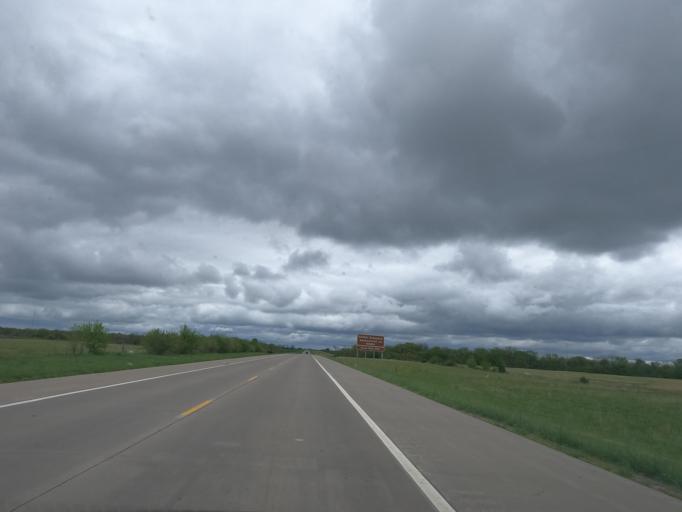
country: US
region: Kansas
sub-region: Labette County
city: Parsons
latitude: 37.3526
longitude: -95.3181
